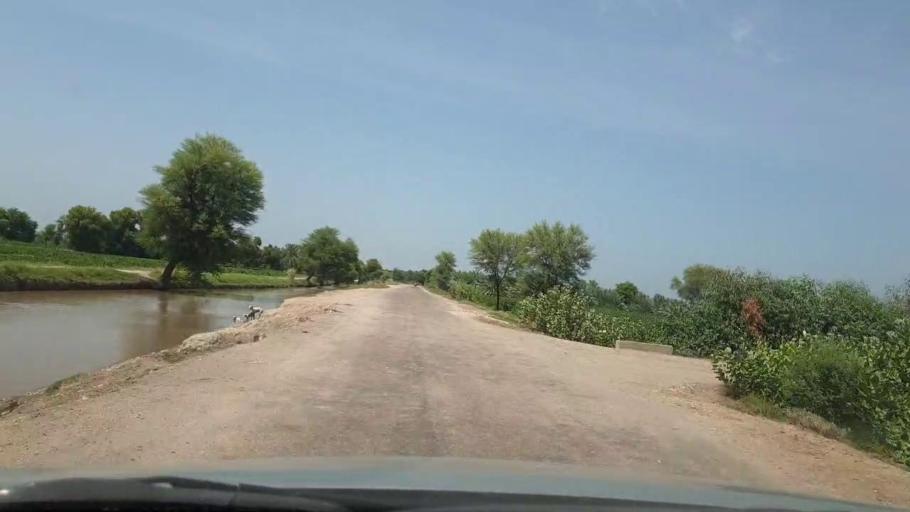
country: PK
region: Sindh
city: Pano Aqil
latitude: 27.6855
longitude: 69.1104
